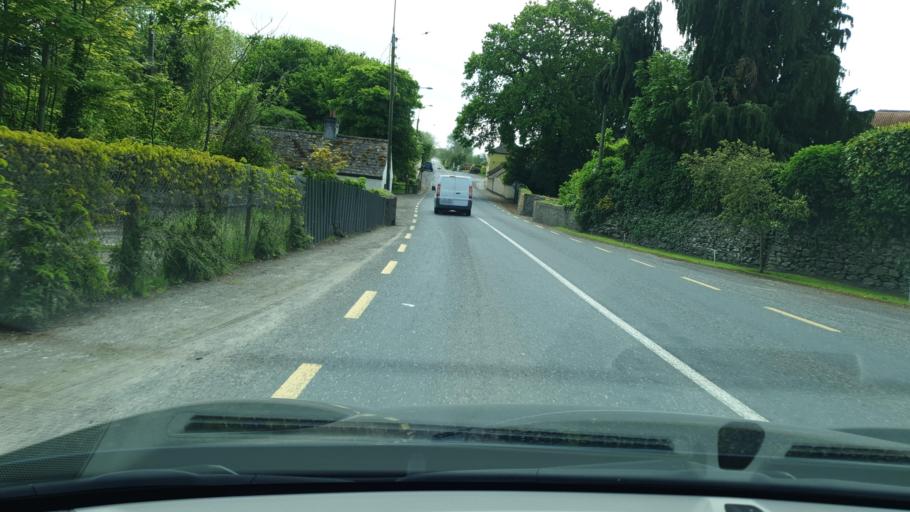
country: IE
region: Leinster
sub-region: An Mhi
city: Navan
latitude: 53.7359
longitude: -6.7123
